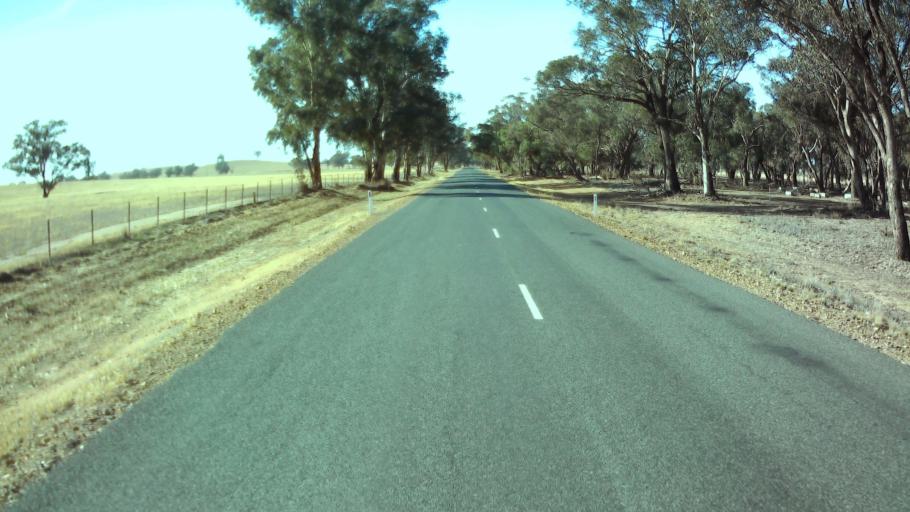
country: AU
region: New South Wales
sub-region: Weddin
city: Grenfell
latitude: -33.9521
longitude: 148.1387
